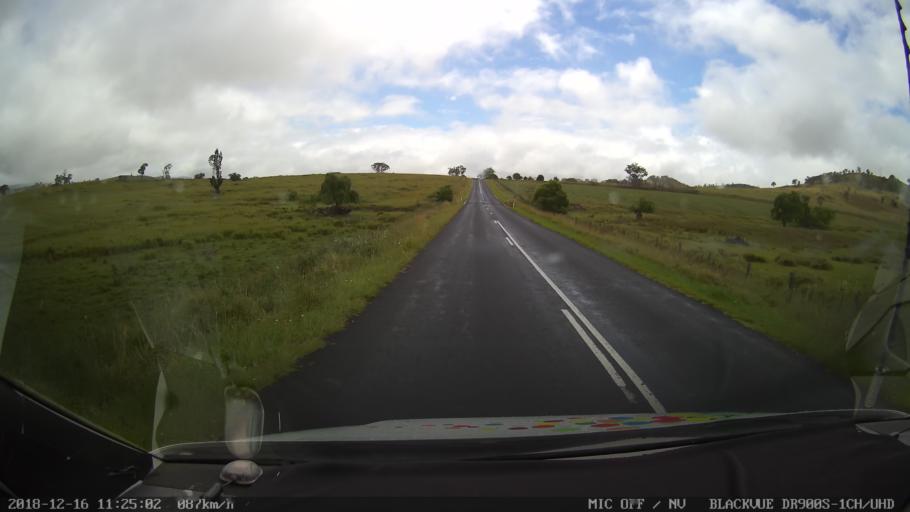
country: AU
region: New South Wales
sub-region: Tenterfield Municipality
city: Carrolls Creek
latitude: -29.0576
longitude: 152.0564
